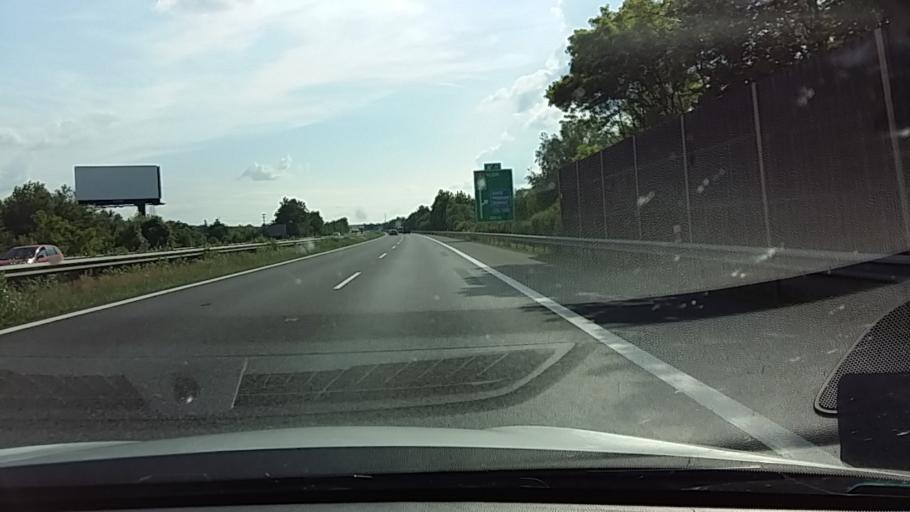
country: CZ
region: Central Bohemia
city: Zdice
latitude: 49.9058
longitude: 13.9697
